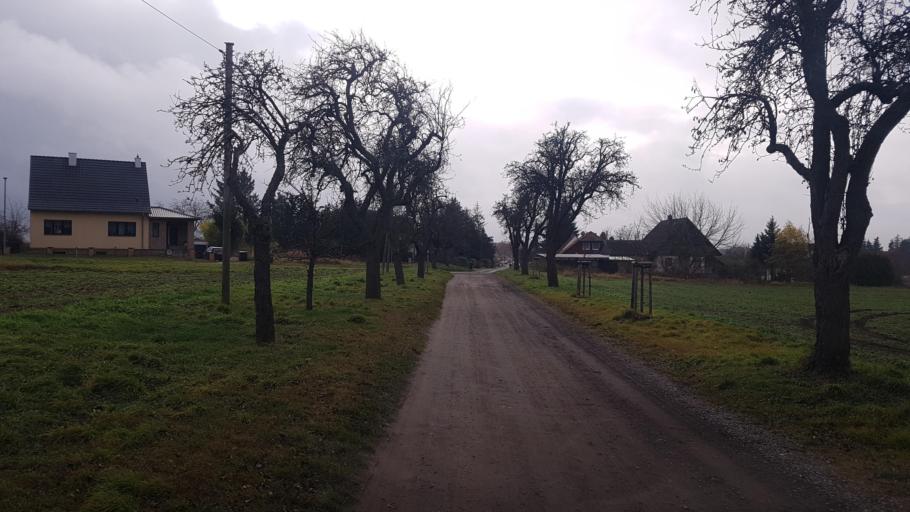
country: DE
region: Brandenburg
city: Roskow
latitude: 52.4243
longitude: 12.7215
